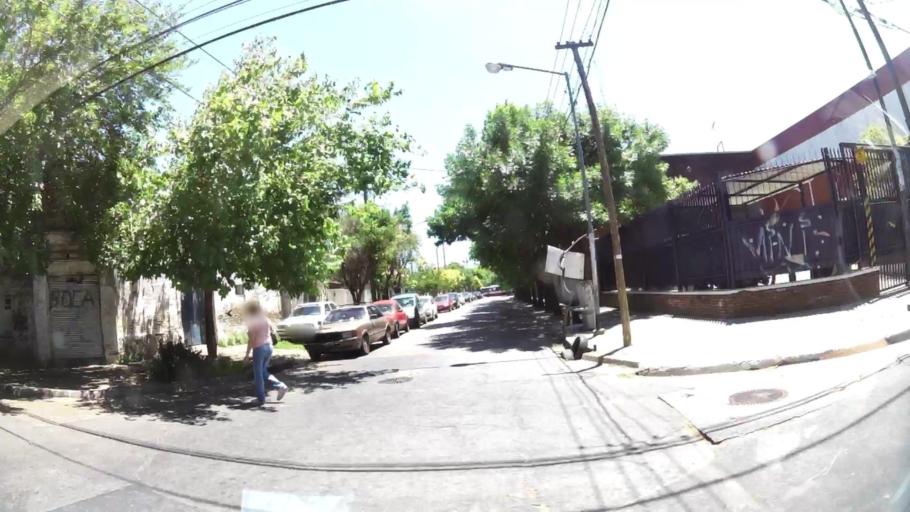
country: AR
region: Buenos Aires
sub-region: Partido de General San Martin
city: General San Martin
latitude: -34.5838
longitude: -58.5446
